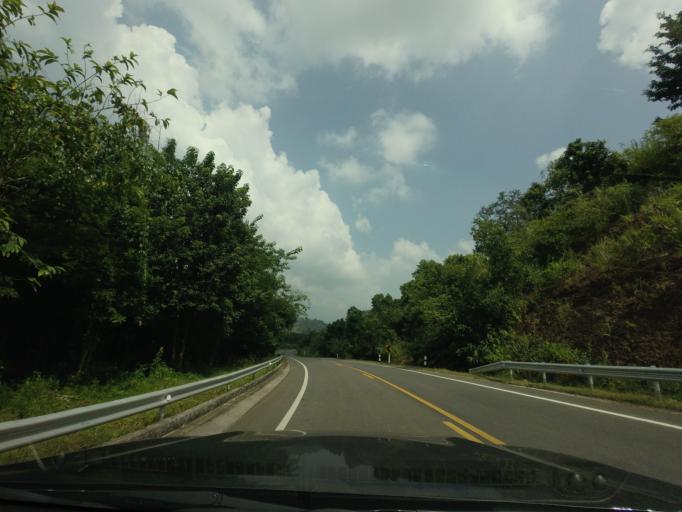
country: TH
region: Nan
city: Santi Suk
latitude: 18.9219
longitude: 100.8935
